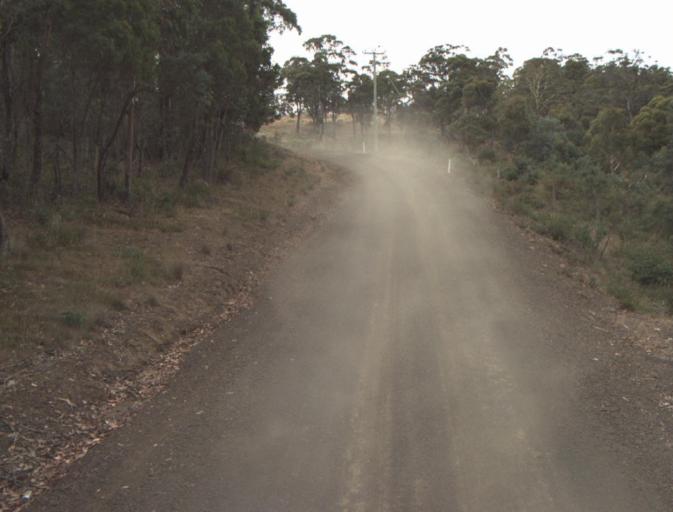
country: AU
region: Tasmania
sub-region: Northern Midlands
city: Evandale
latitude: -41.5208
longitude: 147.4353
